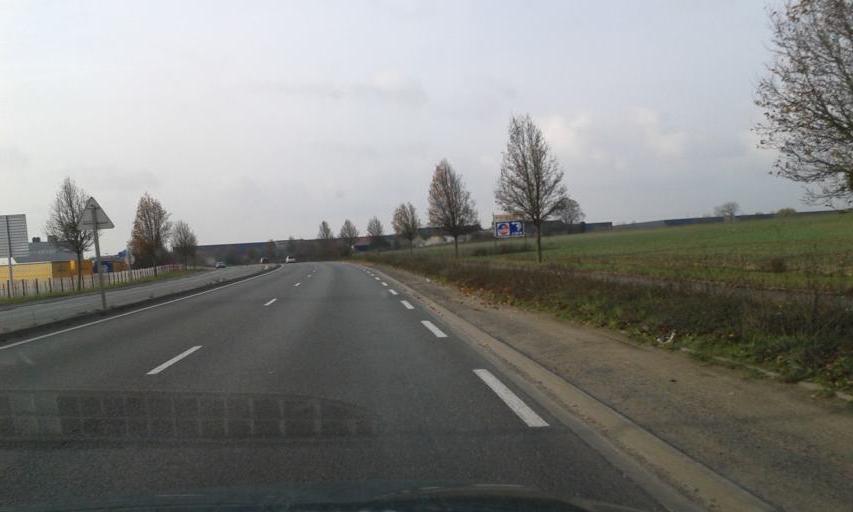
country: FR
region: Centre
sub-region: Departement du Loiret
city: Saran
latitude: 47.9527
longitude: 1.8566
